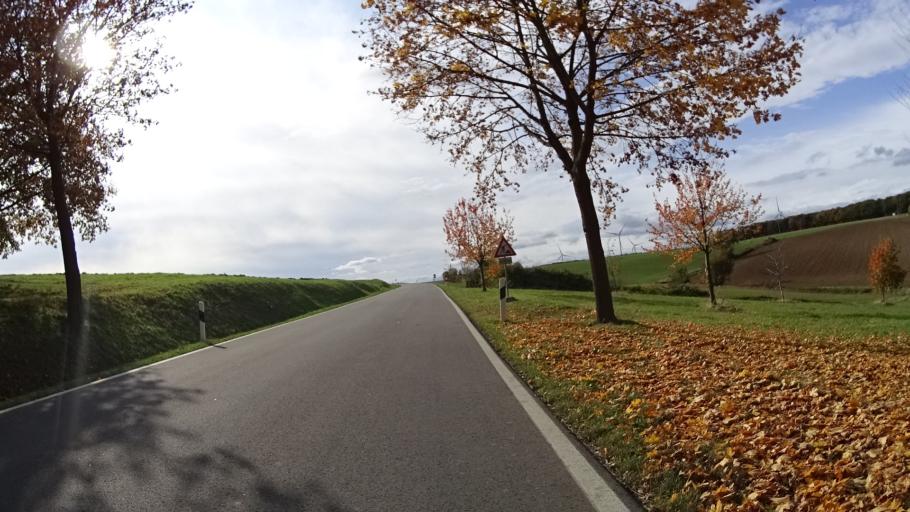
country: DE
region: Rheinland-Pfalz
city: Morsfeld
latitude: 49.7421
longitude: 7.9289
